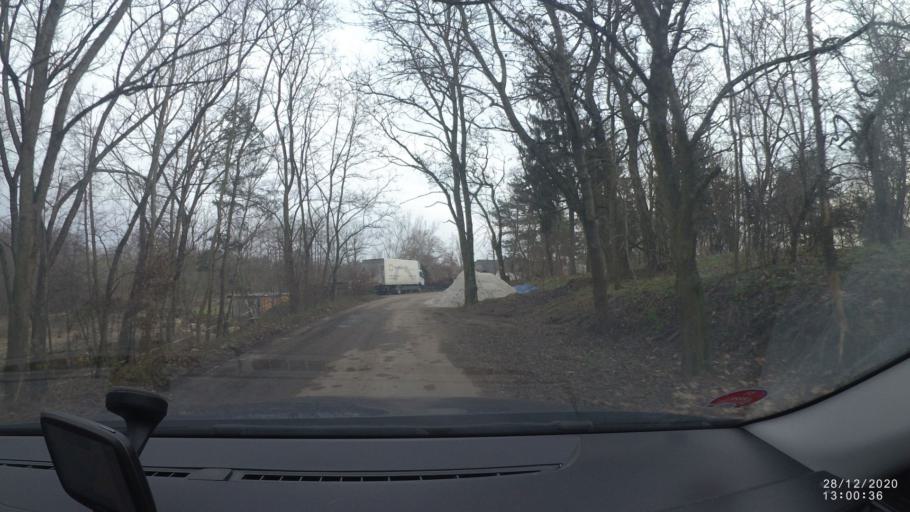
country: CZ
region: Praha
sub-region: Praha 20
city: Horni Pocernice
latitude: 50.1465
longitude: 14.6041
